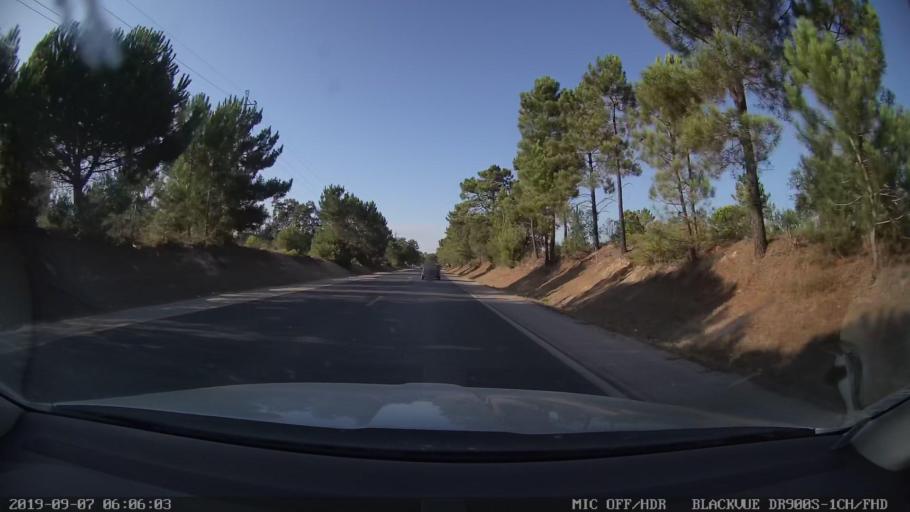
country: PT
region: Setubal
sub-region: Sesimbra
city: Sesimbra
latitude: 38.5074
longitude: -9.1052
